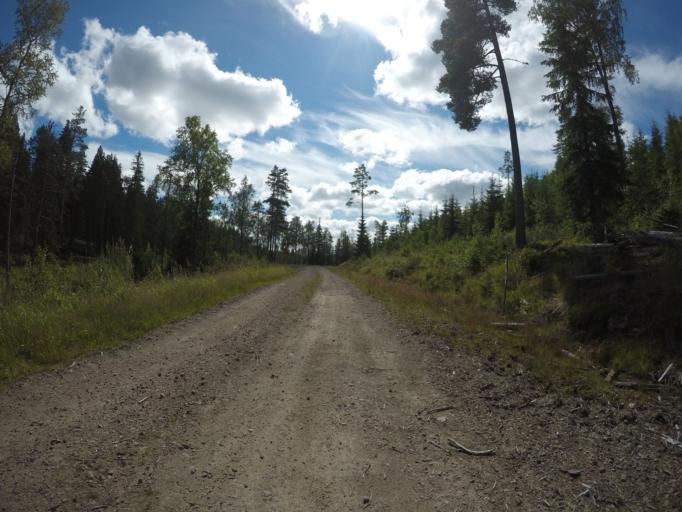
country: SE
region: Vaermland
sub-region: Filipstads Kommun
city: Lesjofors
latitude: 60.0863
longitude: 14.4464
